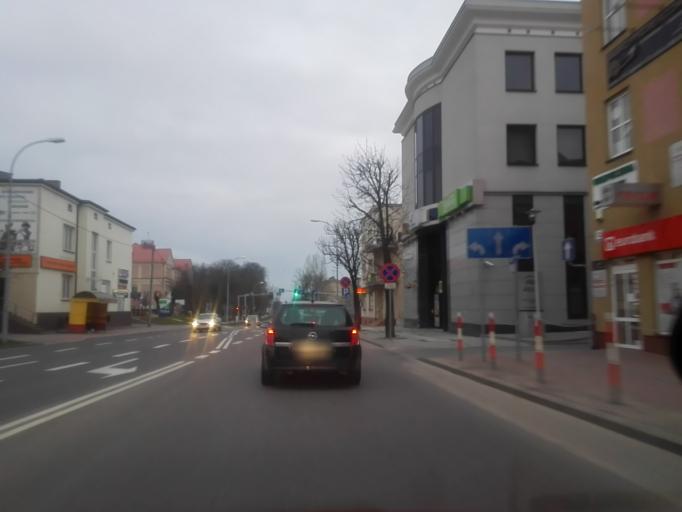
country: PL
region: Podlasie
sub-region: Lomza
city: Lomza
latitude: 53.1777
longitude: 22.0728
